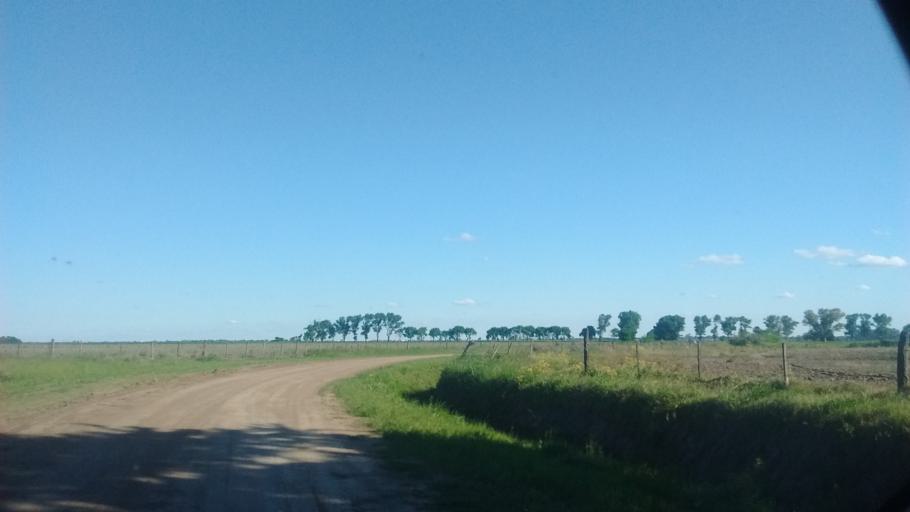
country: AR
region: Santa Fe
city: Funes
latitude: -32.8682
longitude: -60.7986
